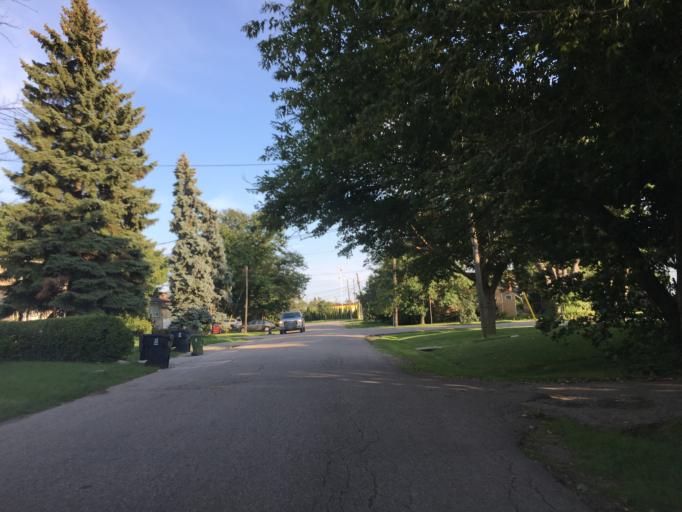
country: CA
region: Ontario
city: Scarborough
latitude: 43.7870
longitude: -79.2816
